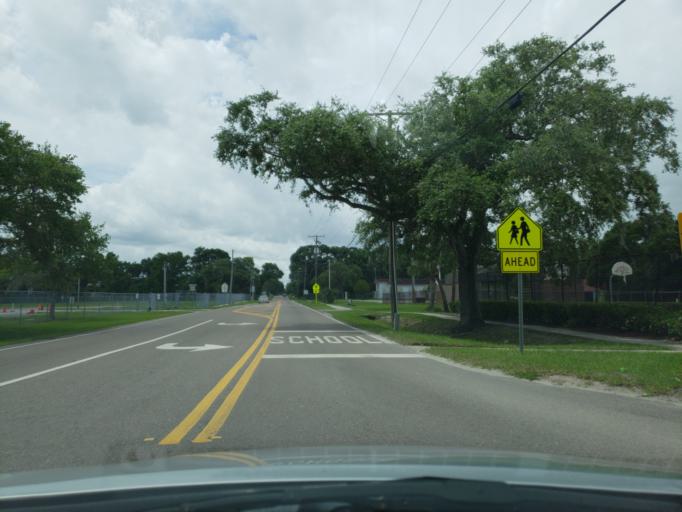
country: US
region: Florida
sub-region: Hillsborough County
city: Temple Terrace
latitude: 28.0103
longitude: -82.4101
